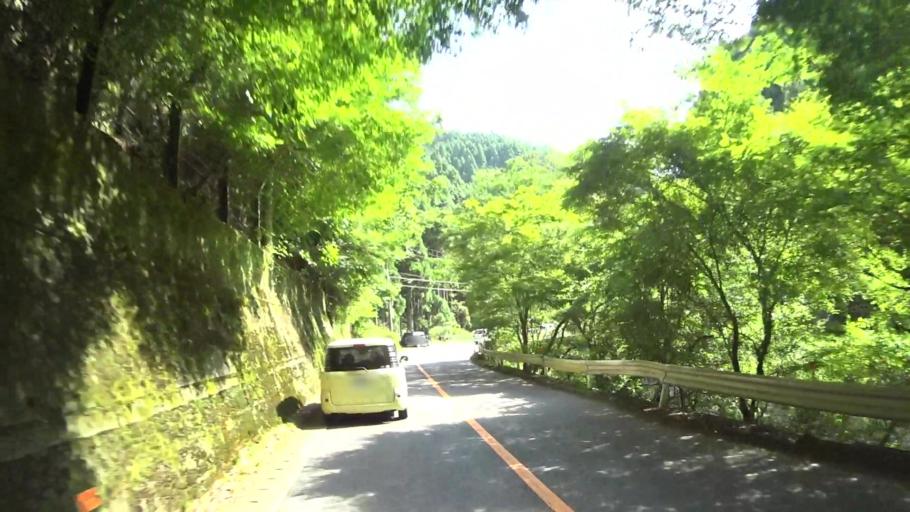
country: JP
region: Kyoto
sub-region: Kyoto-shi
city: Kamigyo-ku
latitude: 35.0650
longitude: 135.6833
